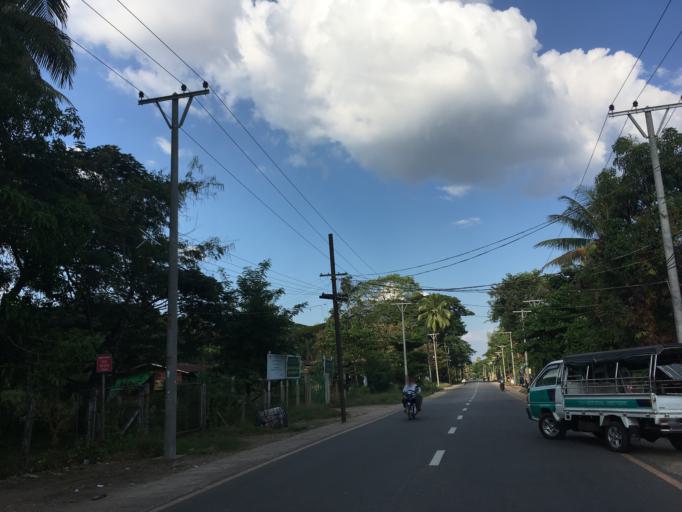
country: MM
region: Mon
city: Mawlamyine
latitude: 16.4467
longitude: 97.6211
